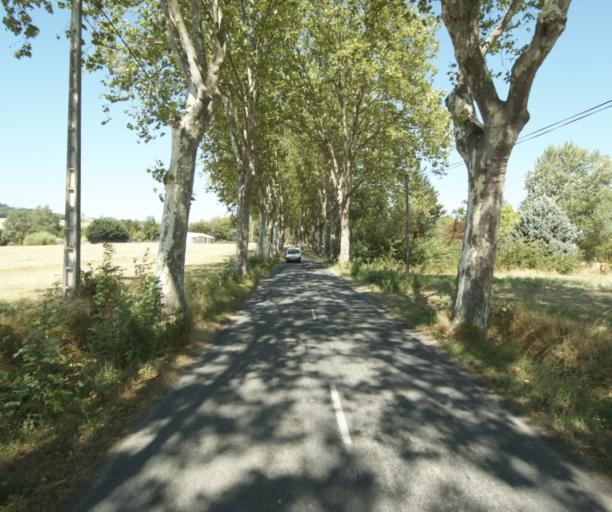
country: FR
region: Midi-Pyrenees
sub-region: Departement de la Haute-Garonne
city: Revel
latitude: 43.5022
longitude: 1.9521
